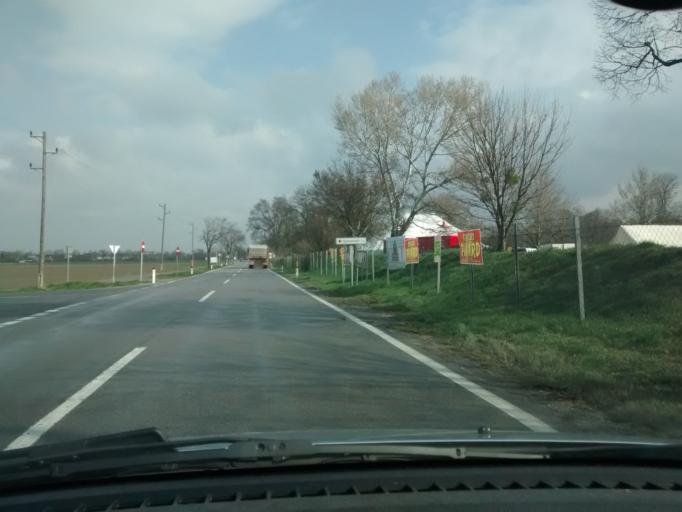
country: AT
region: Lower Austria
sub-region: Politischer Bezirk Modling
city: Laxenburg
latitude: 48.0553
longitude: 16.3517
